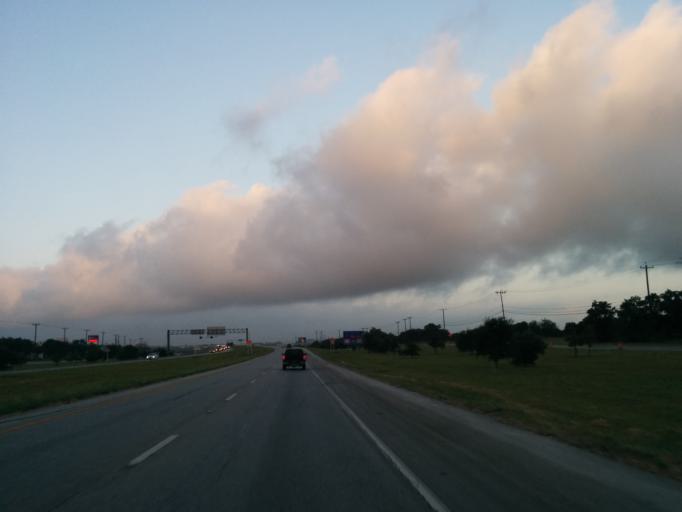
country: US
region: Texas
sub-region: Bexar County
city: Helotes
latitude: 29.5746
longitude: -98.6479
